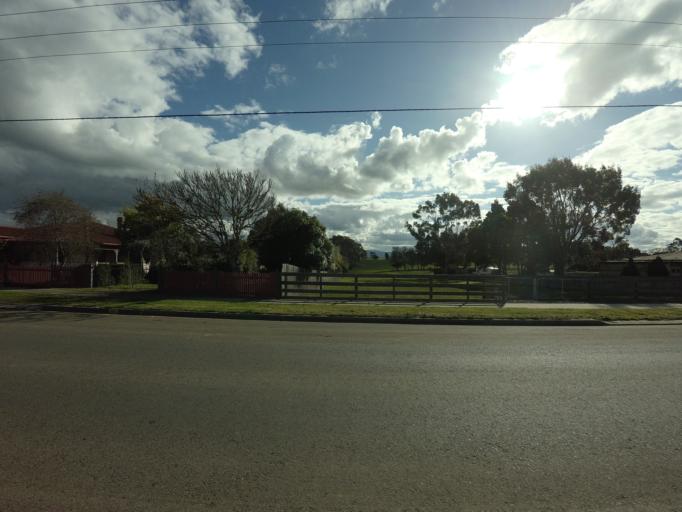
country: AU
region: Tasmania
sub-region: Northern Midlands
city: Longford
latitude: -41.6946
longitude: 147.0784
